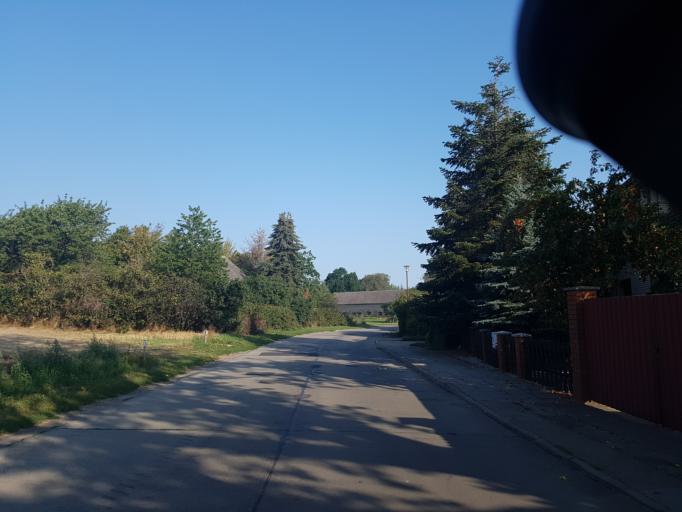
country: DE
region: Brandenburg
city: Niemegk
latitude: 52.0246
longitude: 12.6812
